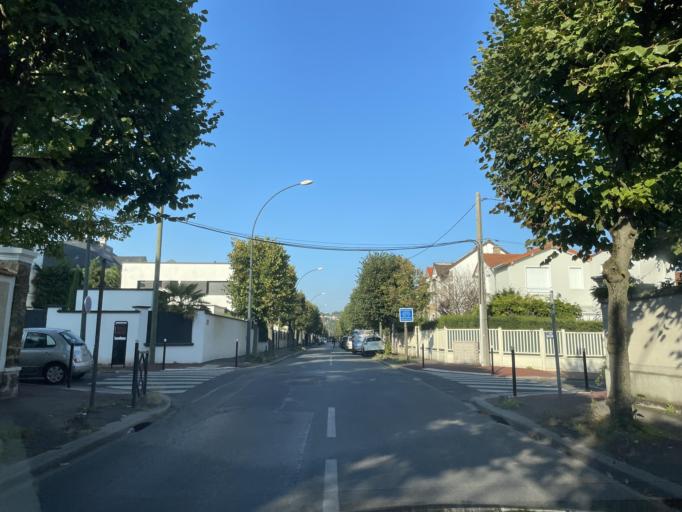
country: FR
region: Ile-de-France
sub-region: Departement du Val-de-Marne
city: Chennevieres-sur-Marne
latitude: 48.7981
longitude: 2.5168
